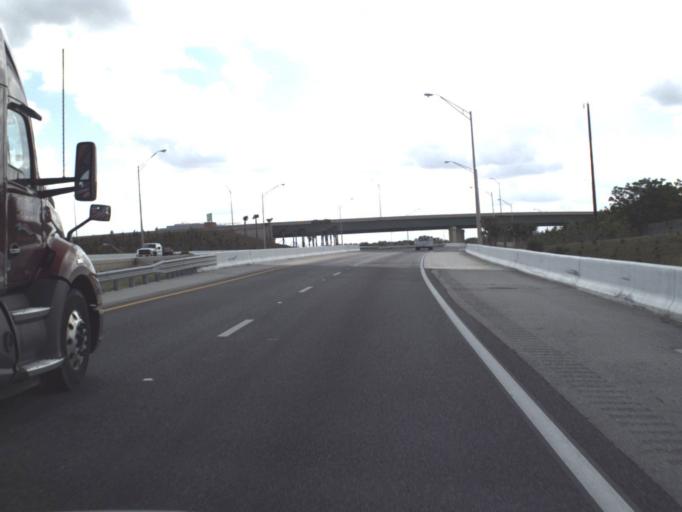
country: US
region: Florida
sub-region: Orange County
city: Paradise Heights
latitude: 28.6532
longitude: -81.5451
